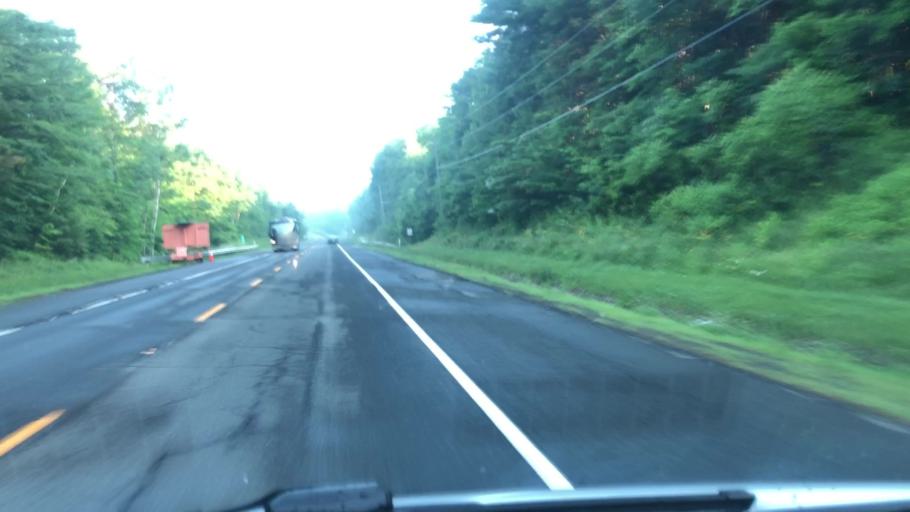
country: US
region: Massachusetts
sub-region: Berkshire County
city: Hinsdale
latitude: 42.4880
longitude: -72.9930
